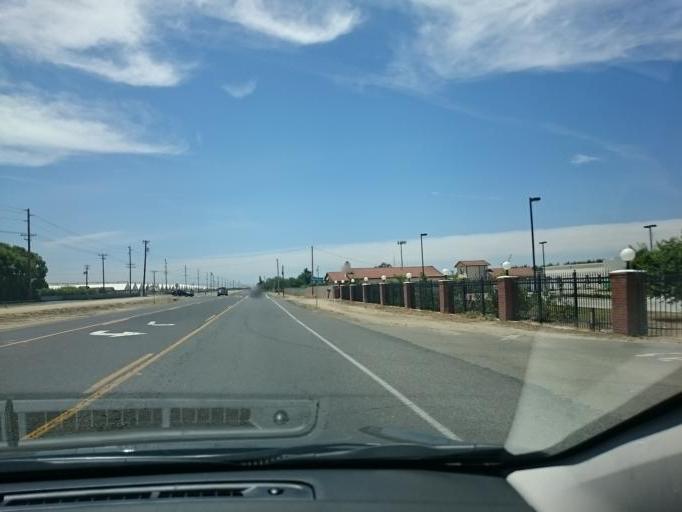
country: US
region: California
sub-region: Stanislaus County
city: Hughson
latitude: 37.6093
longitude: -120.8869
